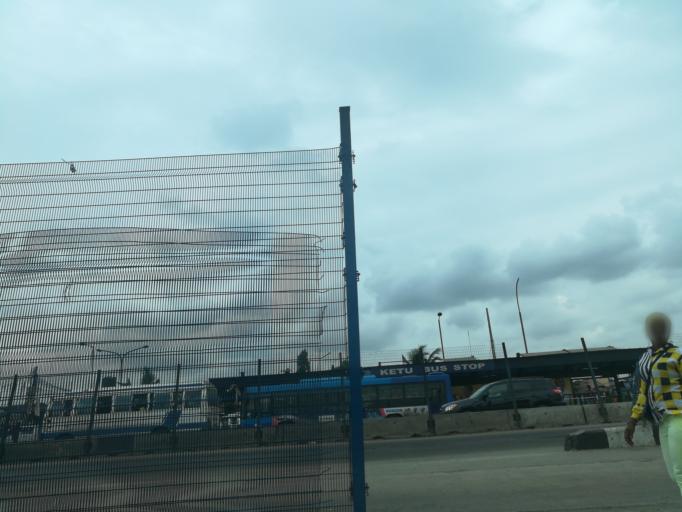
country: NG
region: Lagos
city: Ojota
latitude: 6.5964
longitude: 3.3853
